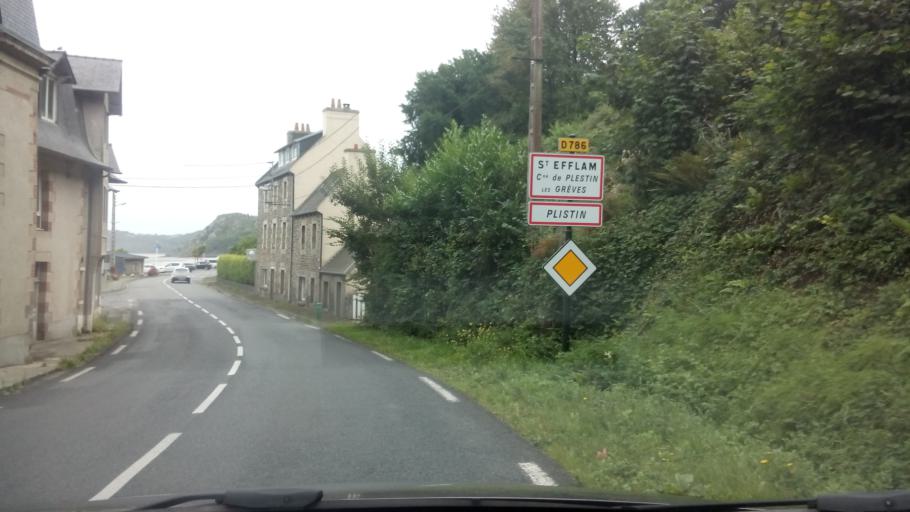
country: FR
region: Brittany
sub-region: Departement des Cotes-d'Armor
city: Plestin-les-Greves
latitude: 48.6691
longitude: -3.6088
